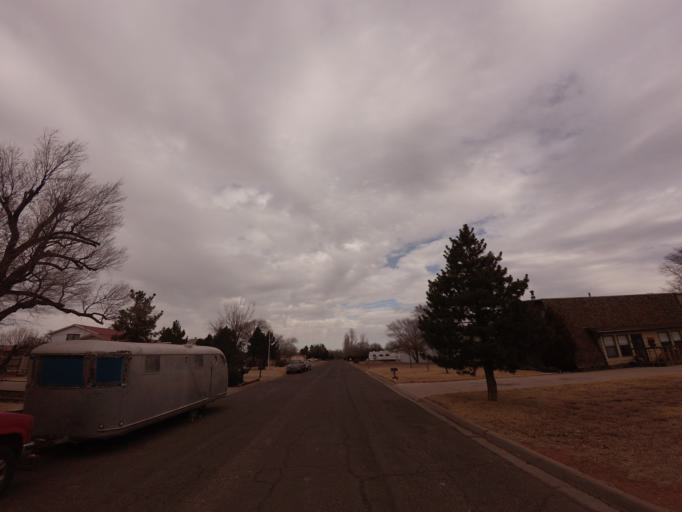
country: US
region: New Mexico
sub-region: Curry County
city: Clovis
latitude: 34.3779
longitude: -103.2022
